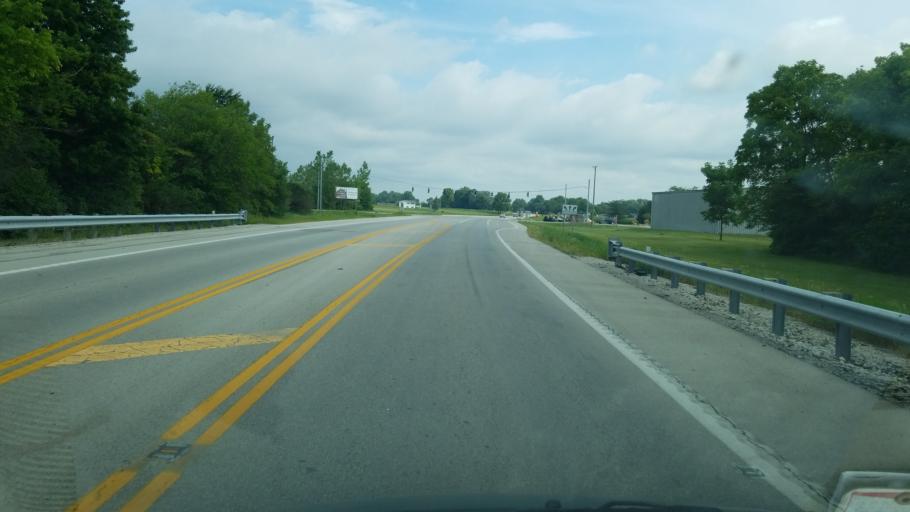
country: US
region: Ohio
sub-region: Sandusky County
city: Ballville
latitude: 41.2900
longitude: -83.1713
